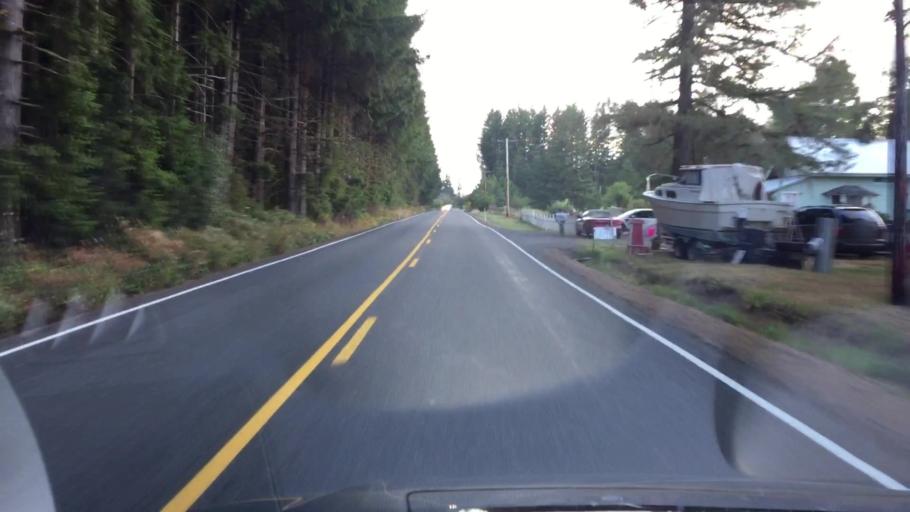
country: US
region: Washington
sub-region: Lewis County
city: Napavine
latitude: 46.4995
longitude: -122.7634
